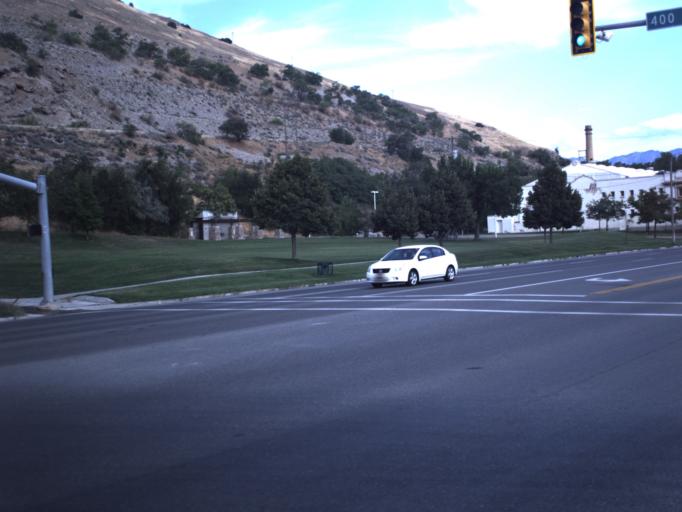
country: US
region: Utah
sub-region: Salt Lake County
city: Salt Lake City
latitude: 40.7901
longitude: -111.9012
